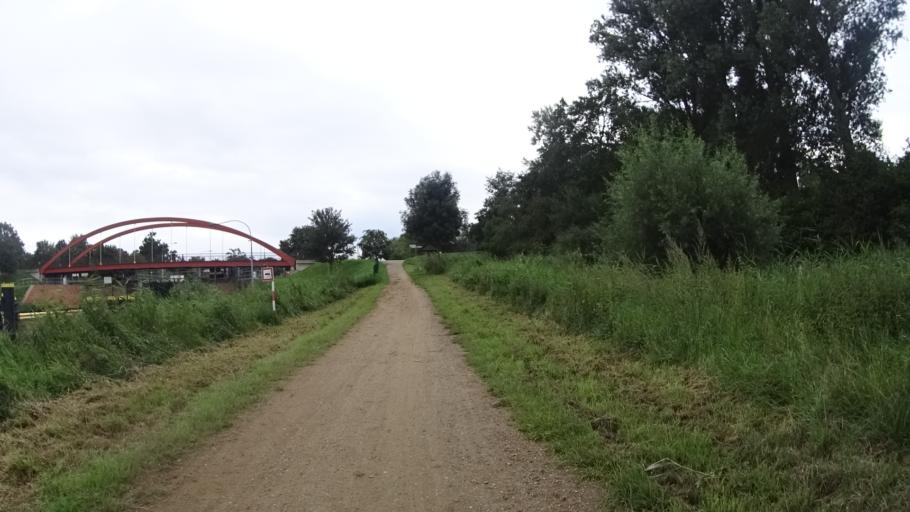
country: DE
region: Schleswig-Holstein
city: Panten
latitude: 53.6736
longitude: 10.6357
